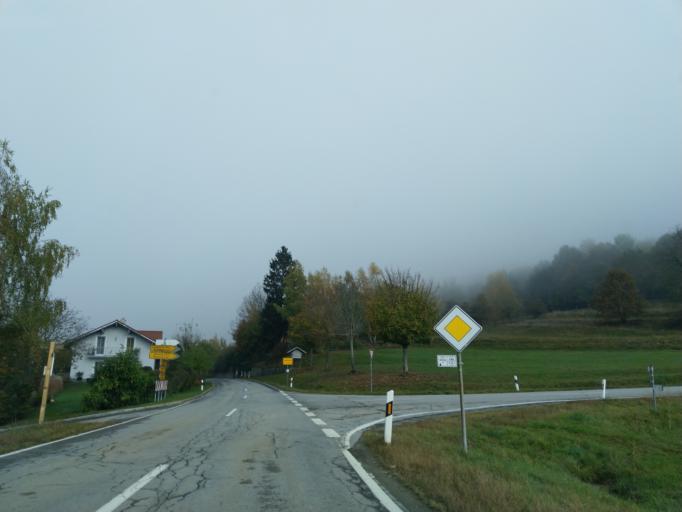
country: DE
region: Bavaria
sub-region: Lower Bavaria
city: Grattersdorf
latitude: 48.8015
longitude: 13.1539
